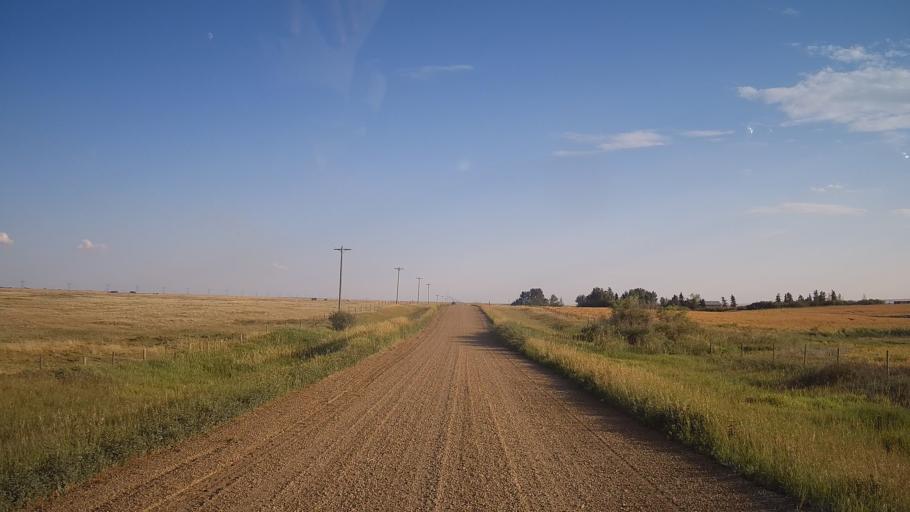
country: CA
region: Alberta
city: Hanna
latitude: 51.6163
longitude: -111.8568
